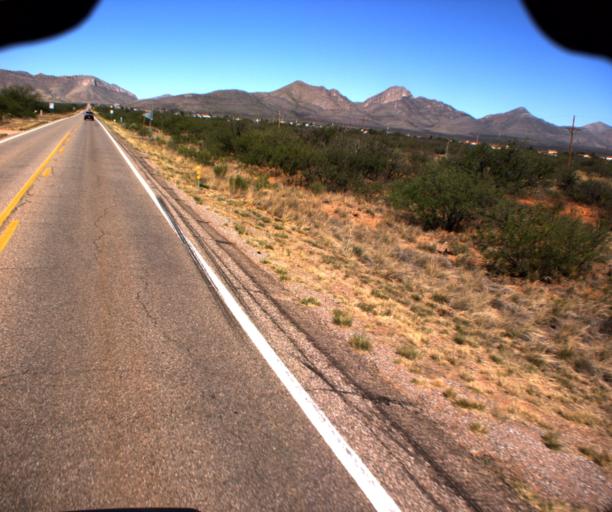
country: US
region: Arizona
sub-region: Cochise County
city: Huachuca City
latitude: 31.6926
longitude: -110.3591
